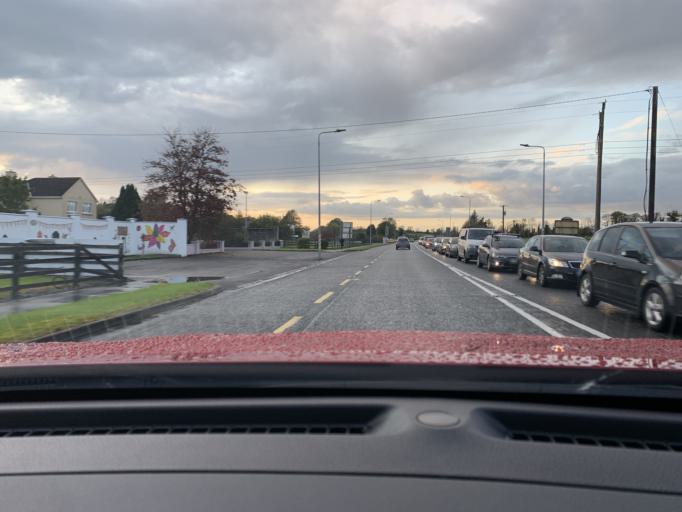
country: IE
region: Connaught
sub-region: County Leitrim
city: Carrick-on-Shannon
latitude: 53.9430
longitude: -8.1099
